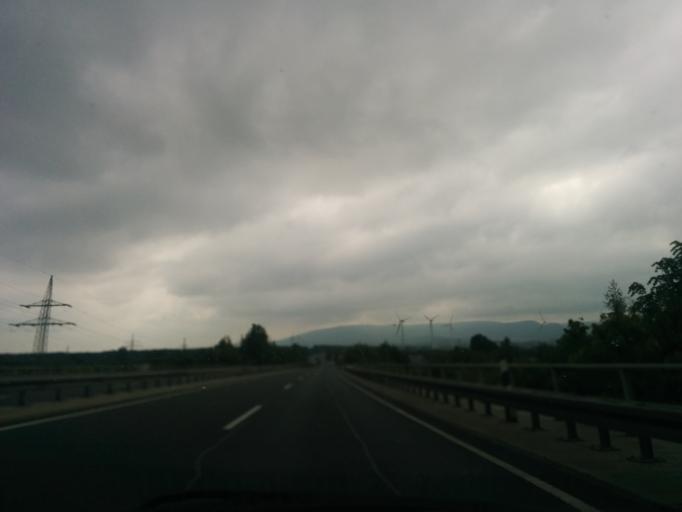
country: DE
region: Lower Saxony
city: Goslar
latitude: 51.9305
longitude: 10.4938
